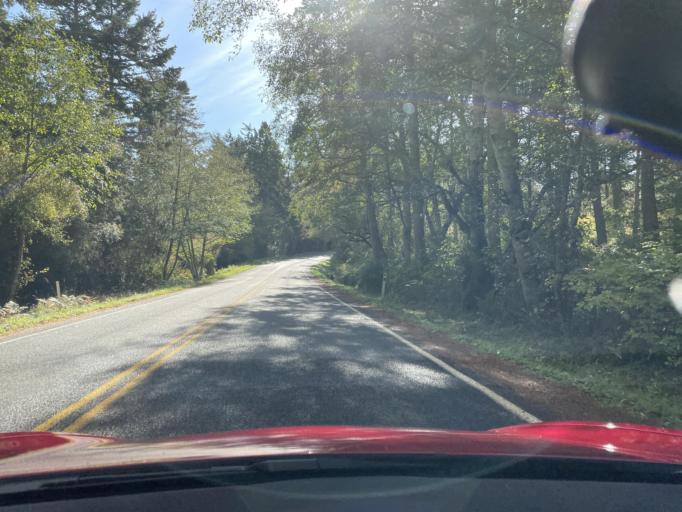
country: US
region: Washington
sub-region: San Juan County
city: Friday Harbor
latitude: 48.4688
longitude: -123.0314
